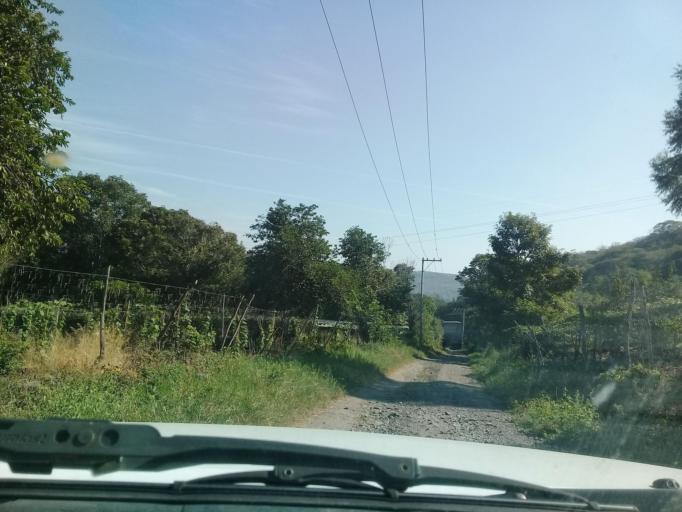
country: MX
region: Veracruz
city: Actopan
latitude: 19.4966
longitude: -96.6108
